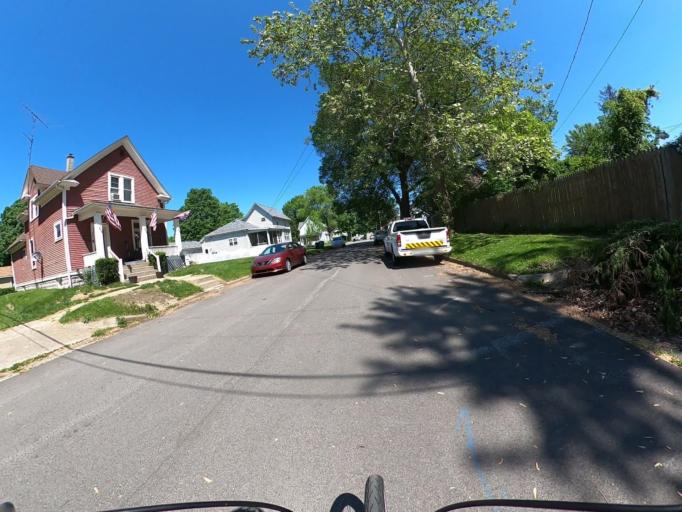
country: US
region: Indiana
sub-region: LaPorte County
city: LaPorte
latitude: 41.6047
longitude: -86.7224
